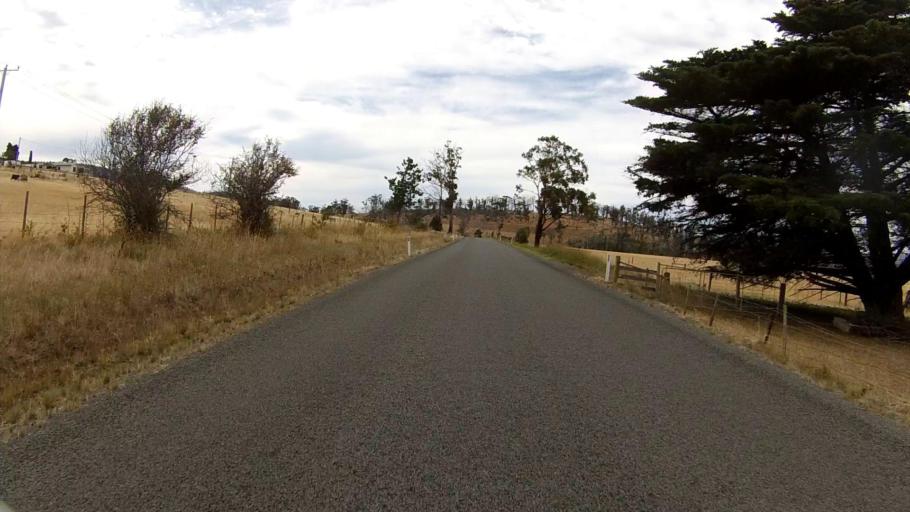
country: AU
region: Tasmania
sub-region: Sorell
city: Sorell
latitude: -42.8963
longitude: 147.7723
